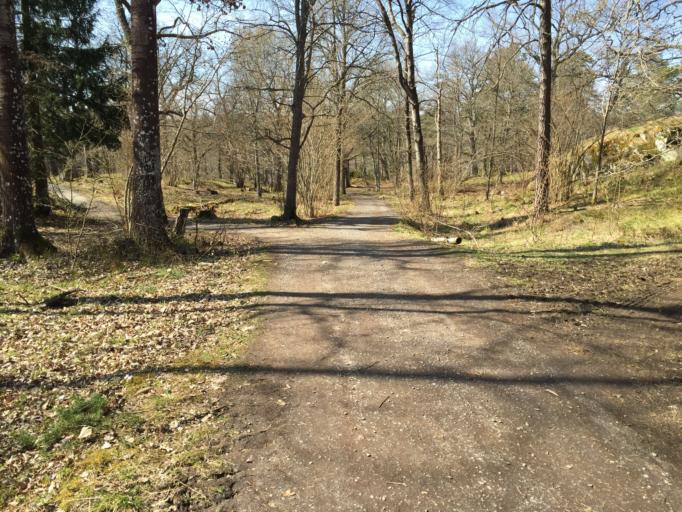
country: SE
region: Stockholm
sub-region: Nacka Kommun
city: Alta
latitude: 59.2699
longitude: 18.1524
